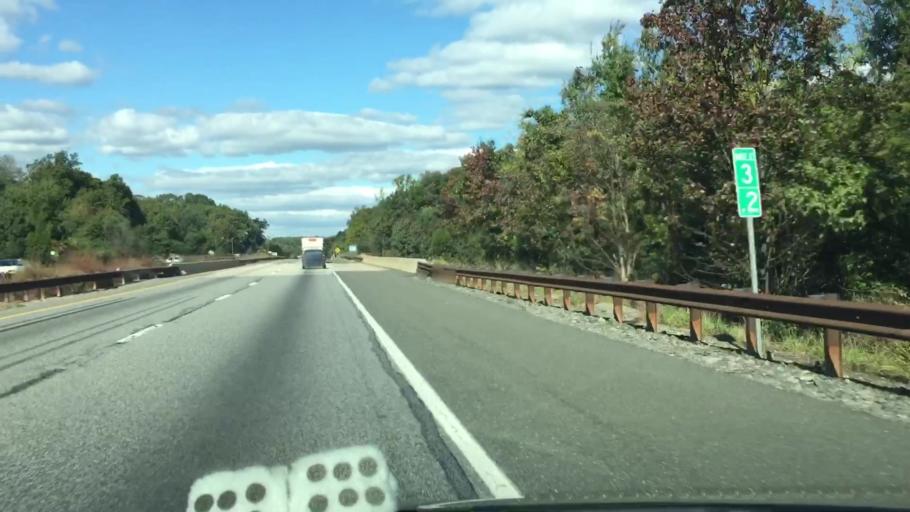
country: US
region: Pennsylvania
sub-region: Delaware County
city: Swarthmore
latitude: 39.9123
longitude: -75.3621
